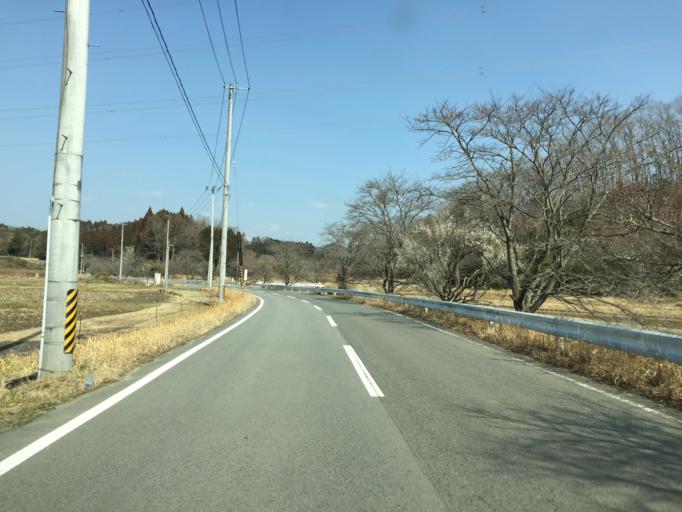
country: JP
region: Fukushima
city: Iwaki
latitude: 36.9648
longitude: 140.7563
